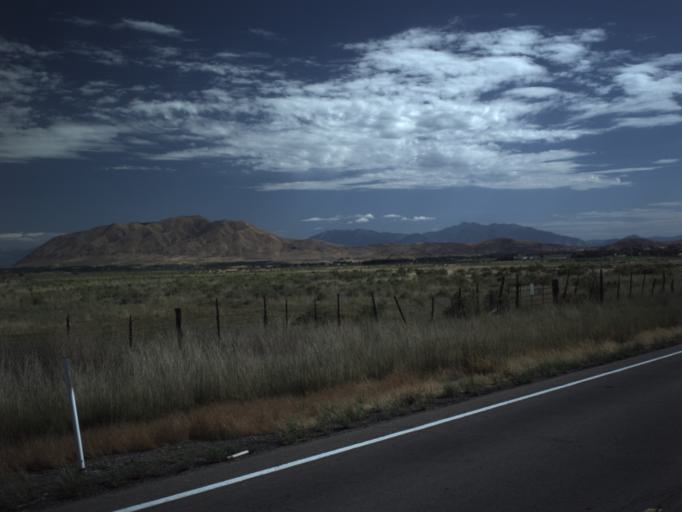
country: US
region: Utah
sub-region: Utah County
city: Genola
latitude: 39.9546
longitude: -111.8884
